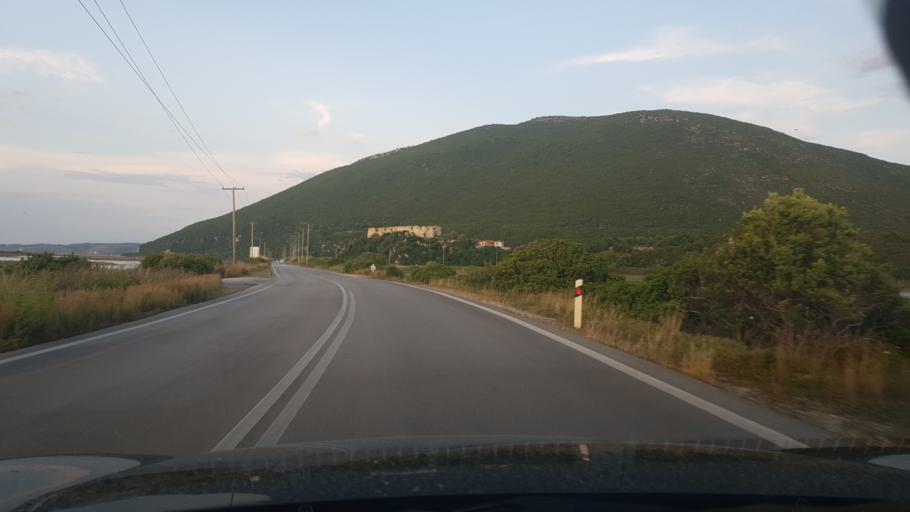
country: GR
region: Ionian Islands
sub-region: Lefkada
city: Lefkada
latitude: 38.8460
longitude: 20.7337
